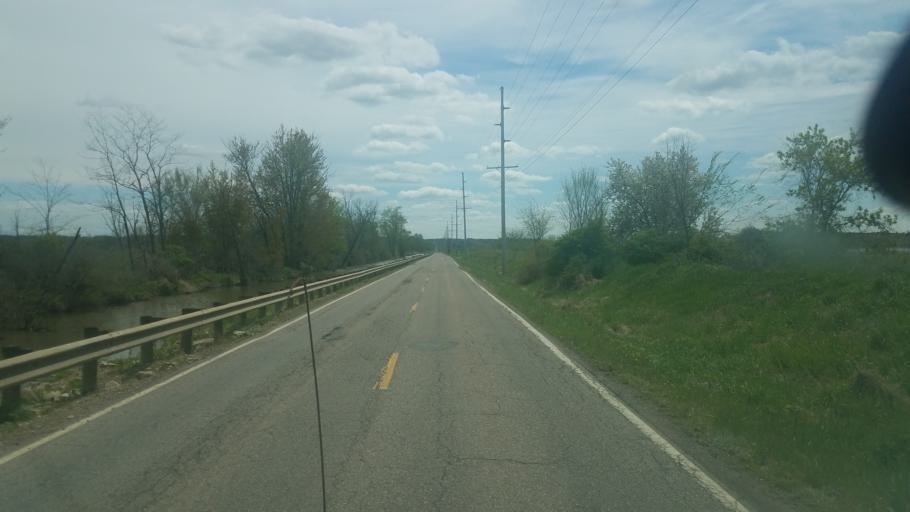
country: US
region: Ohio
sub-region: Wayne County
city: Wooster
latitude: 40.7628
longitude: -81.9443
